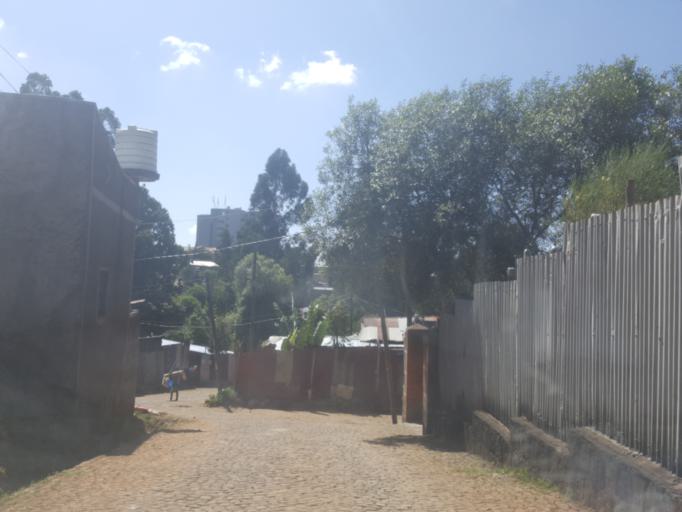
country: ET
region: Adis Abeba
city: Addis Ababa
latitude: 9.0710
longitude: 38.7341
